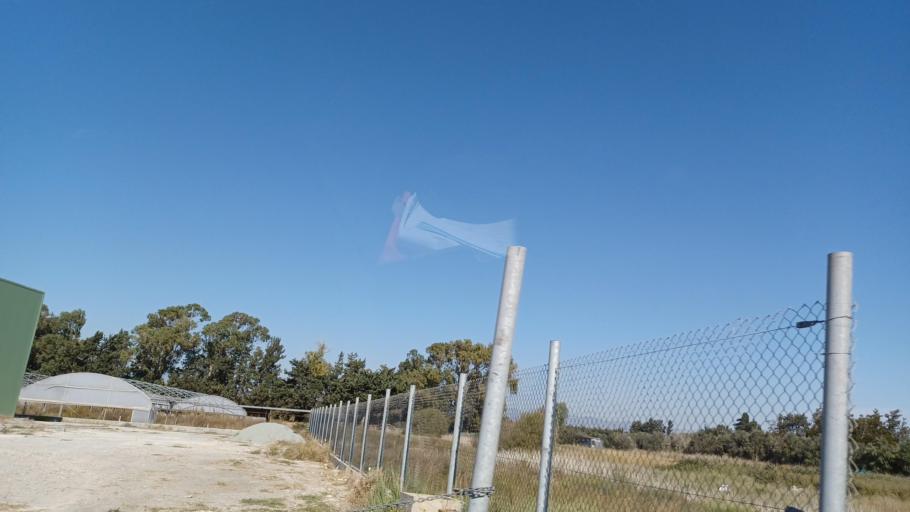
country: CY
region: Larnaka
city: Kolossi
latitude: 34.6322
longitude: 32.9356
